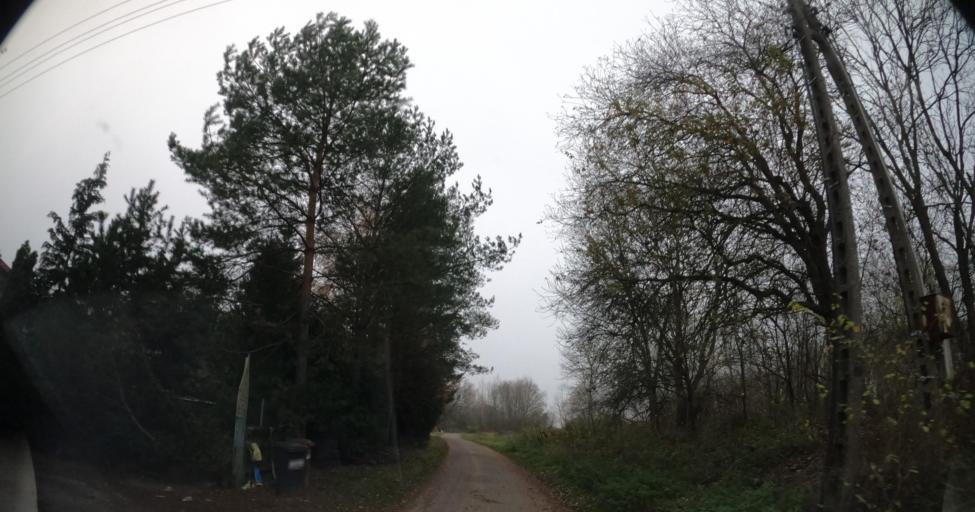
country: PL
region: West Pomeranian Voivodeship
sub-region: Powiat drawski
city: Drawsko Pomorskie
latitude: 53.5777
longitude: 15.8147
